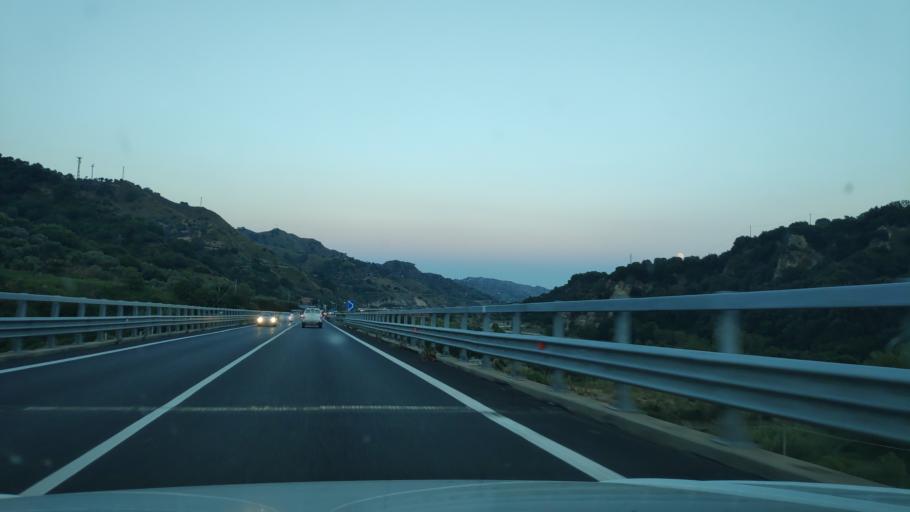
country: IT
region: Calabria
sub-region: Provincia di Reggio Calabria
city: Mammola
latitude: 38.3588
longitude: 16.2212
